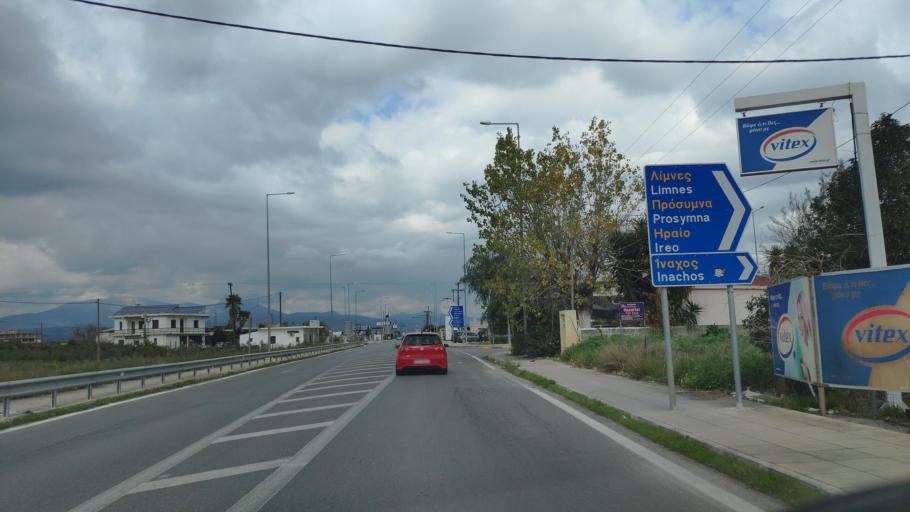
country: GR
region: Peloponnese
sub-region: Nomos Argolidos
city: Argos
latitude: 37.6490
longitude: 22.7292
